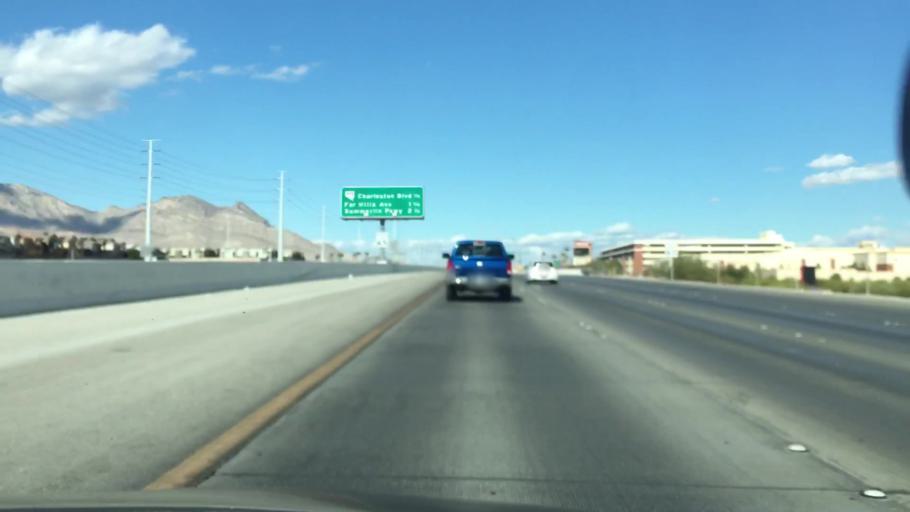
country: US
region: Nevada
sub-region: Clark County
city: Summerlin South
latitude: 36.1512
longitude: -115.3368
